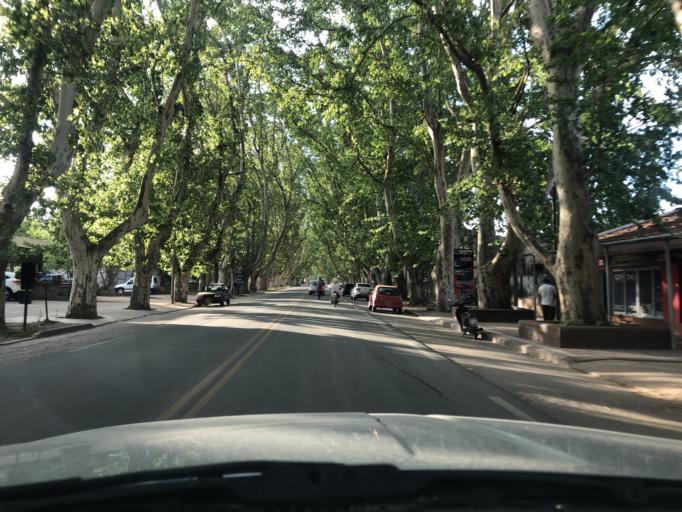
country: AR
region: Cordoba
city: Jesus Maria
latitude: -31.0039
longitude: -64.0821
